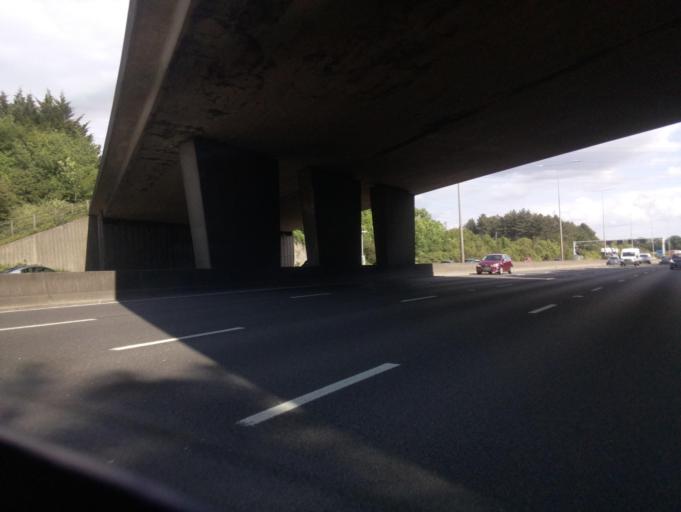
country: GB
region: England
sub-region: Hertfordshire
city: Abbots Langley
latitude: 51.7409
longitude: -0.4003
